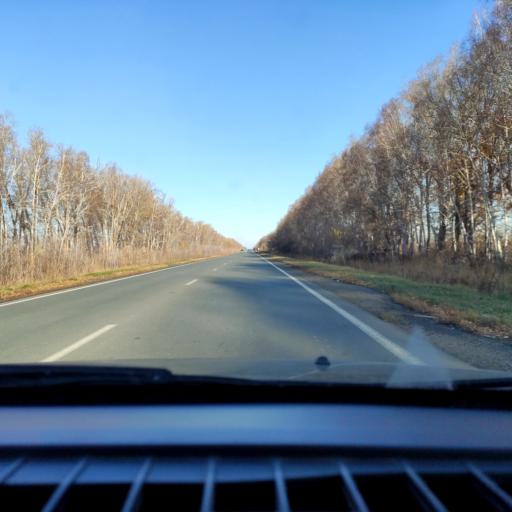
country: RU
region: Samara
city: Tol'yatti
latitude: 53.6031
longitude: 49.3211
